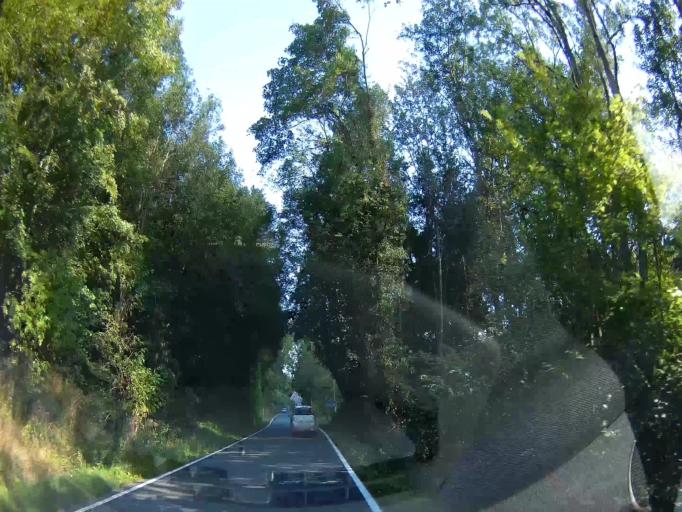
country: BE
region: Wallonia
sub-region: Province de Namur
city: Onhaye
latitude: 50.3076
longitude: 4.7661
